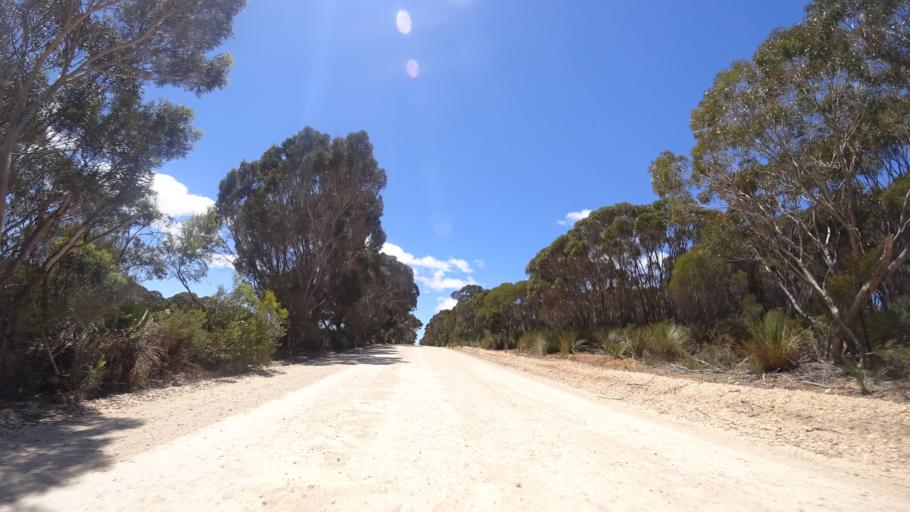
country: AU
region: South Australia
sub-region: Kangaroo Island
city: Kingscote
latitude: -35.8264
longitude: 138.0048
